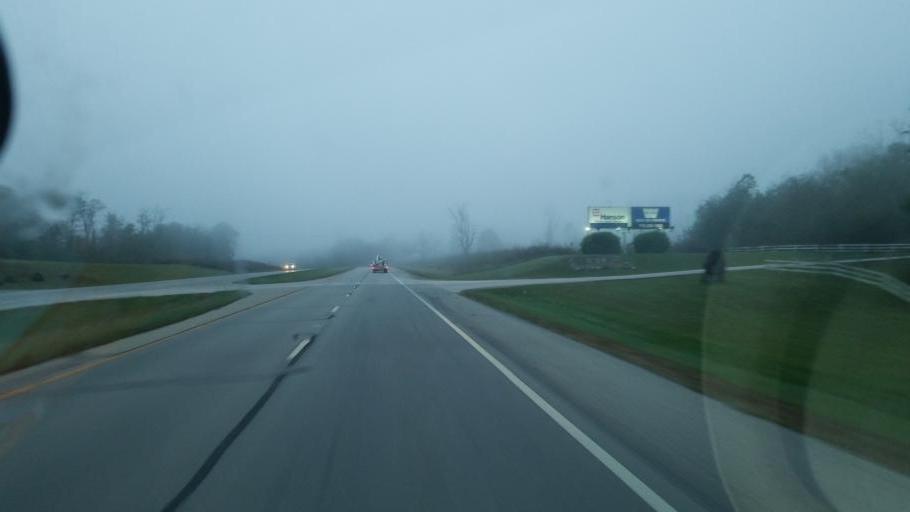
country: US
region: Ohio
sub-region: Pike County
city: Piketon
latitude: 39.0049
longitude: -83.0268
